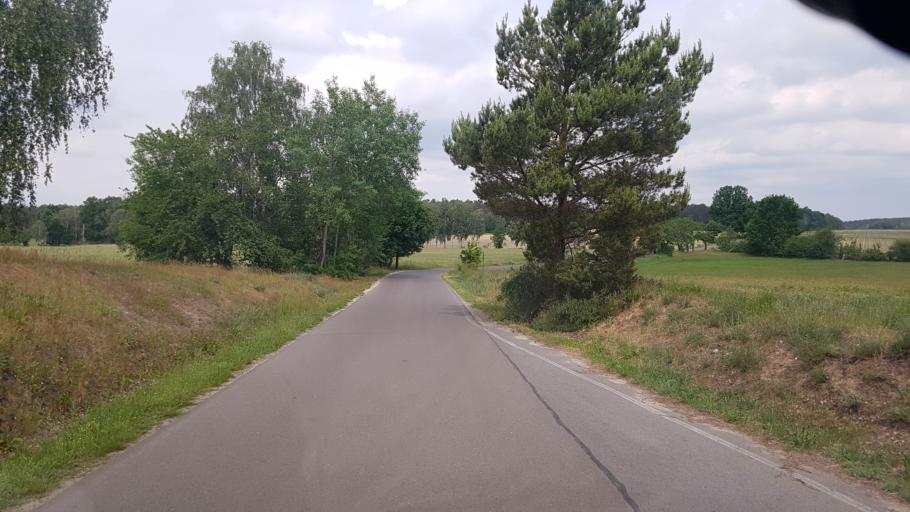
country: DE
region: Brandenburg
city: Lebusa
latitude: 51.8268
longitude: 13.4480
